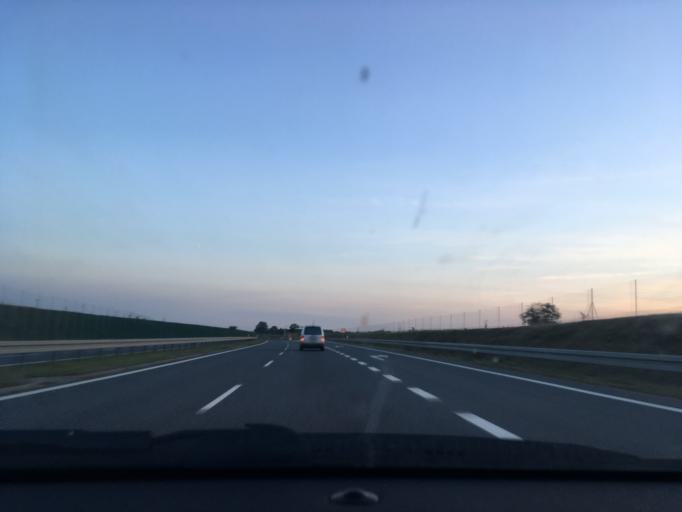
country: PL
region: Podlasie
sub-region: Powiat zambrowski
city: Zambrow
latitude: 52.9860
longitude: 22.2168
